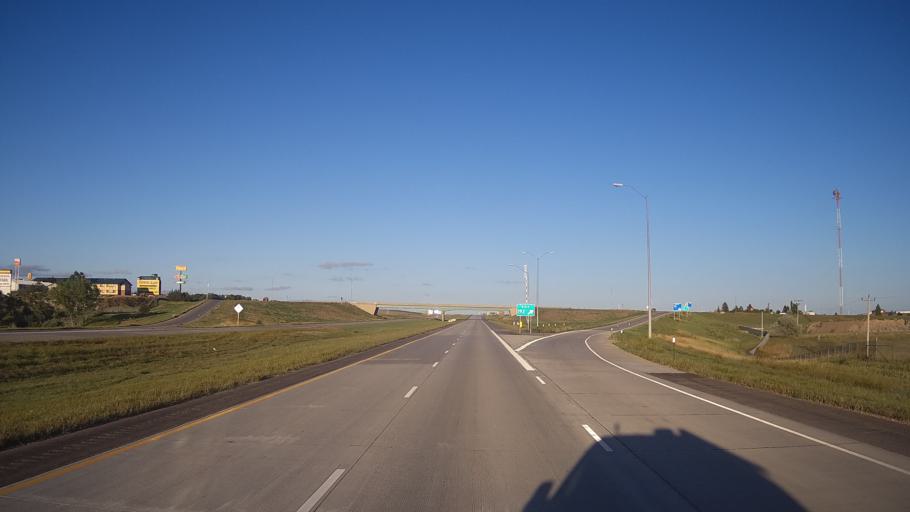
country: US
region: South Dakota
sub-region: Jones County
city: Murdo
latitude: 43.8830
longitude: -100.7110
